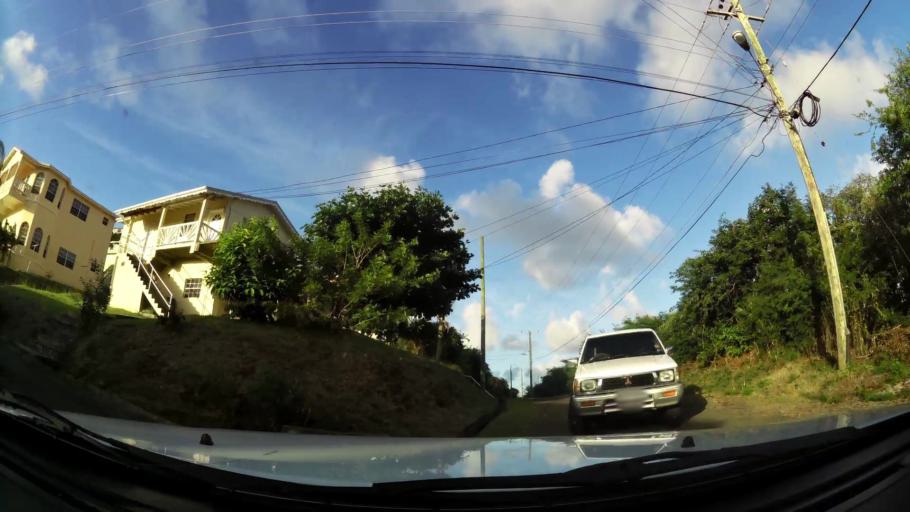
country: LC
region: Gros-Islet
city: Gros Islet
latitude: 14.0750
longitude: -60.9266
